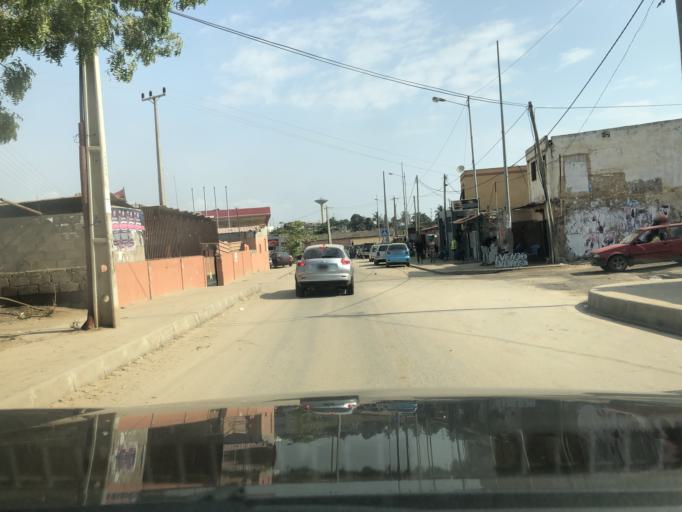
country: AO
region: Luanda
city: Luanda
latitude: -8.8500
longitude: 13.2578
